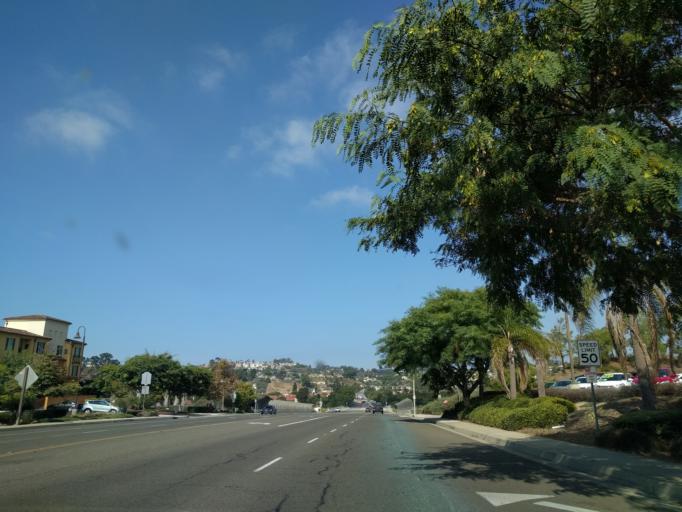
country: US
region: California
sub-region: Orange County
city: Dana Point
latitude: 33.4736
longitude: -117.6762
